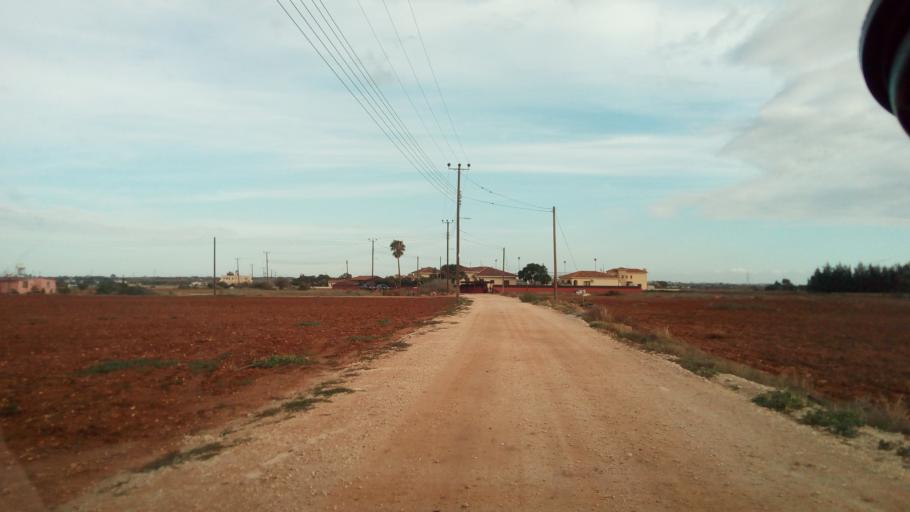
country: CY
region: Ammochostos
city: Avgorou
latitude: 35.0573
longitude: 33.8724
